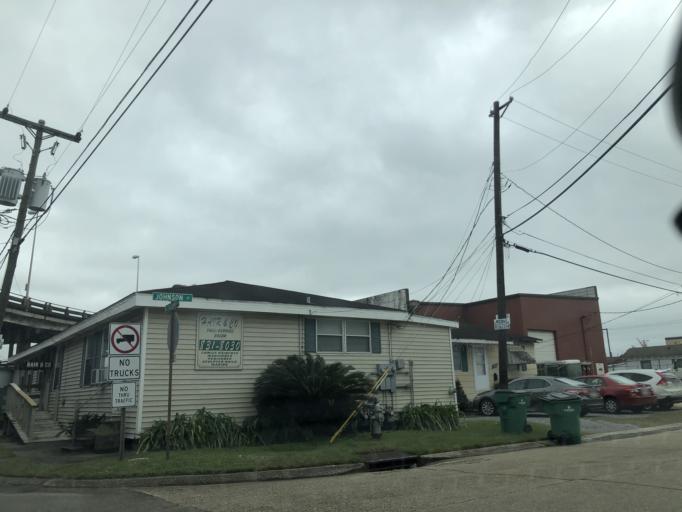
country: US
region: Louisiana
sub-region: Jefferson Parish
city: Metairie Terrace
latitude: 29.9758
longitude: -90.1566
